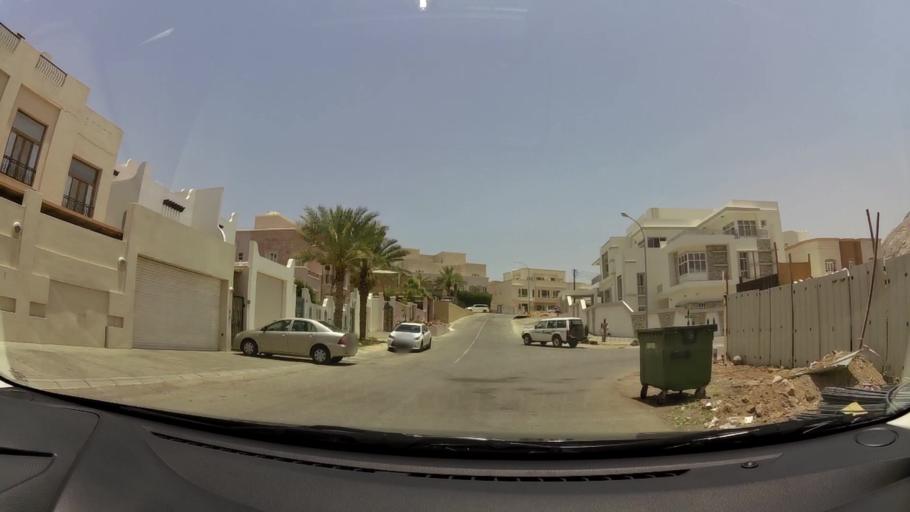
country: OM
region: Muhafazat Masqat
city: Bawshar
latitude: 23.5558
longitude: 58.4146
